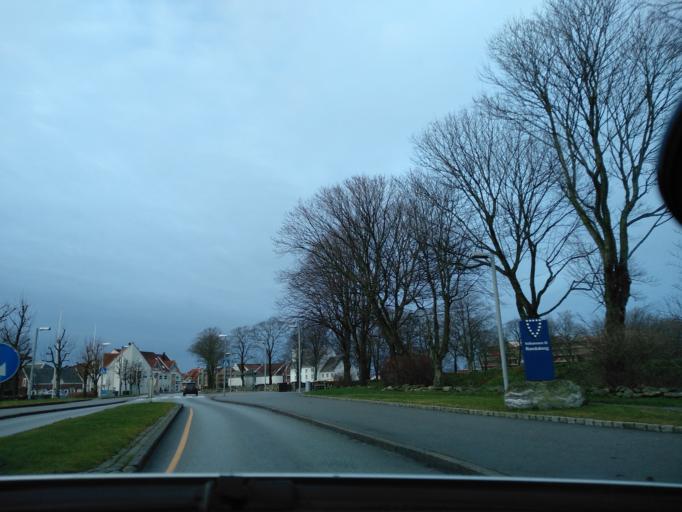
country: NO
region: Rogaland
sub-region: Randaberg
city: Randaberg
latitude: 58.9990
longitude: 5.6222
